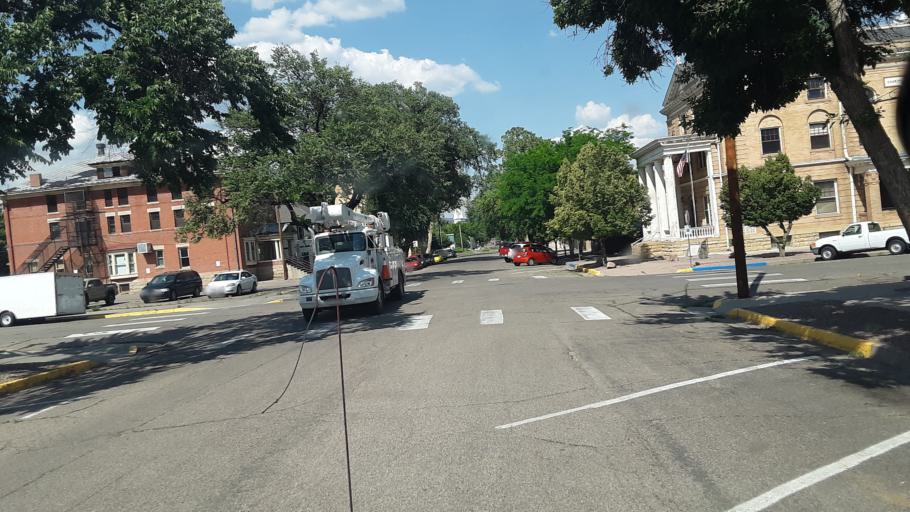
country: US
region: Colorado
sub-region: Fremont County
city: Canon City
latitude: 38.4405
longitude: -105.2430
